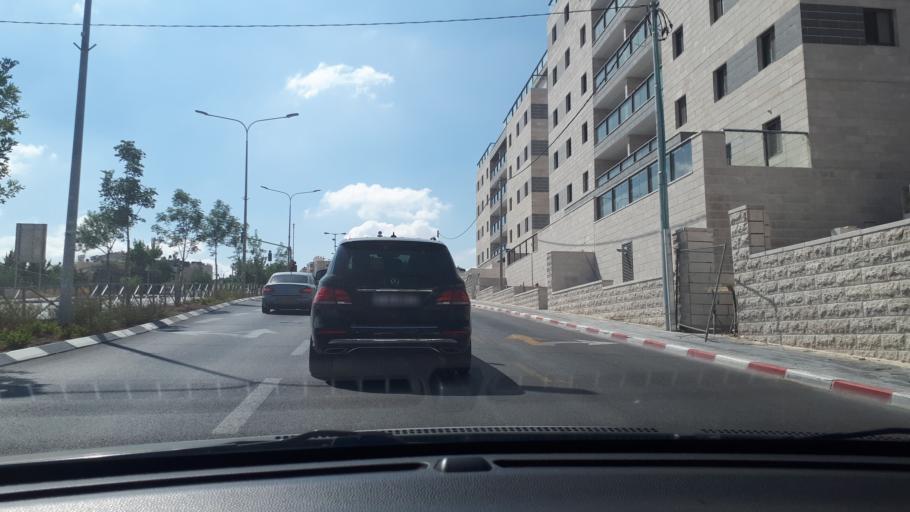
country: PS
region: West Bank
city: Ar Ram wa Dahiyat al Barid
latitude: 31.8262
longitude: 35.2388
